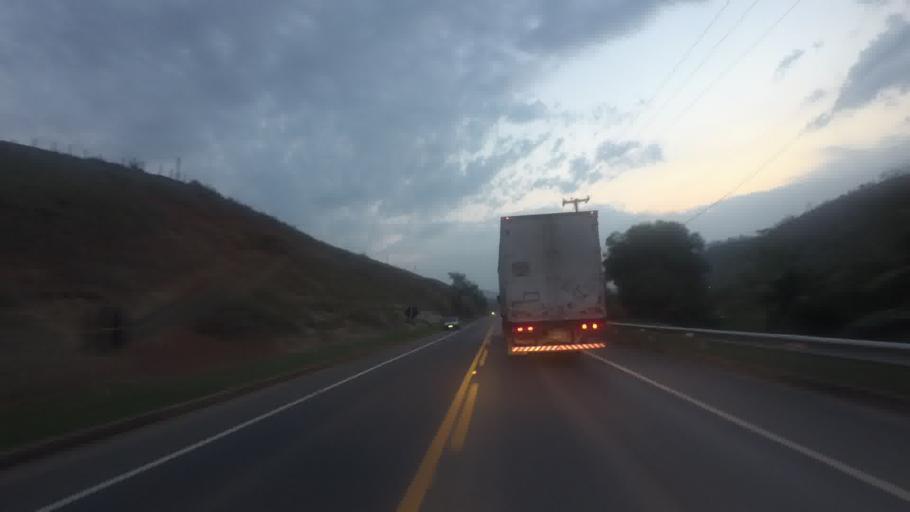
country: BR
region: Minas Gerais
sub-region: Alem Paraiba
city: Alem Paraiba
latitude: -21.8984
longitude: -42.7198
